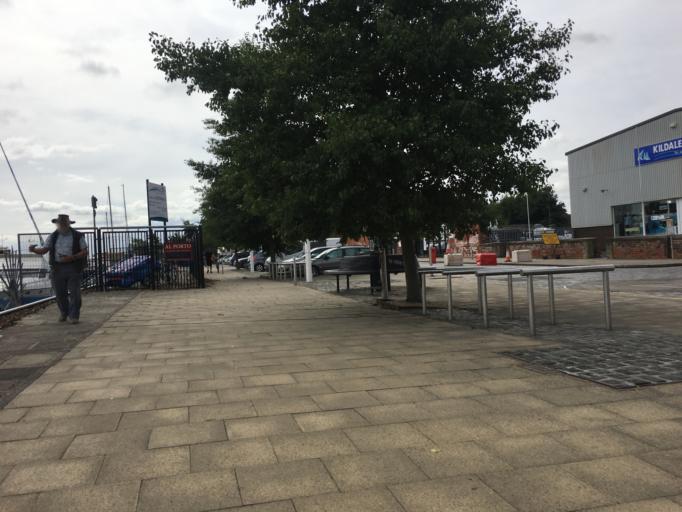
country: GB
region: England
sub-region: City of Kingston upon Hull
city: Hull
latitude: 53.7398
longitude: -0.3388
